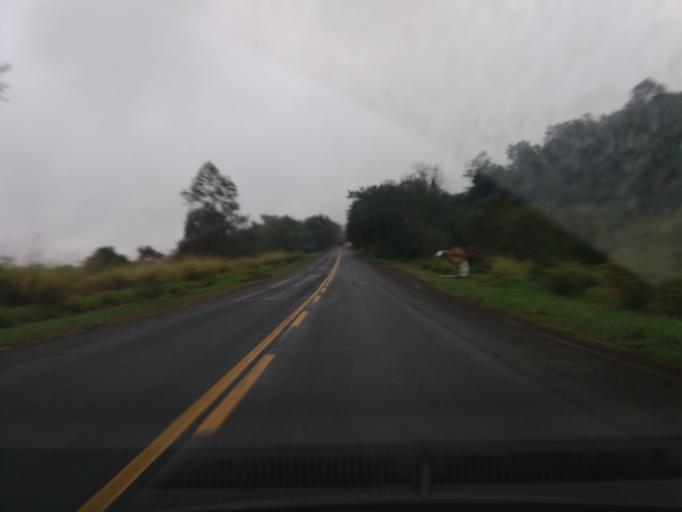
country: BR
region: Parana
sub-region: Ampere
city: Ampere
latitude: -25.8641
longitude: -53.4919
